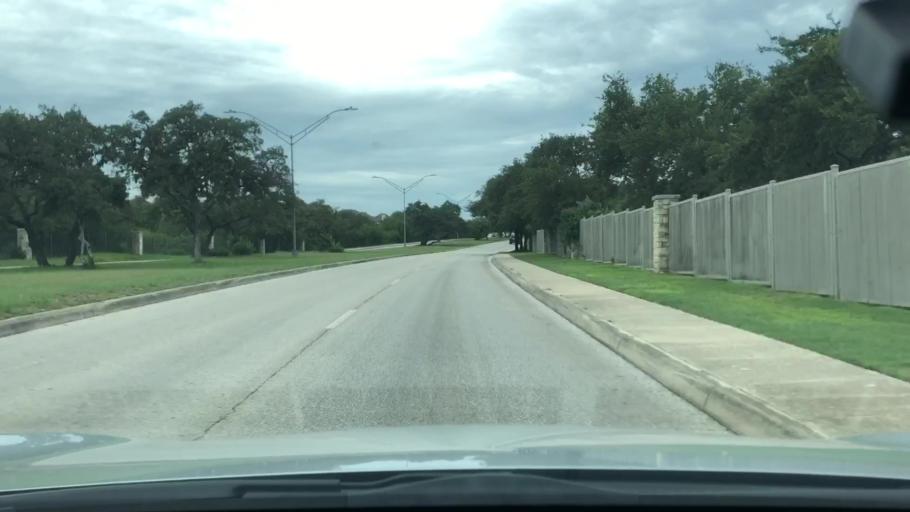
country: US
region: Texas
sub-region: Bexar County
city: Leon Valley
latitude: 29.4618
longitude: -98.6732
